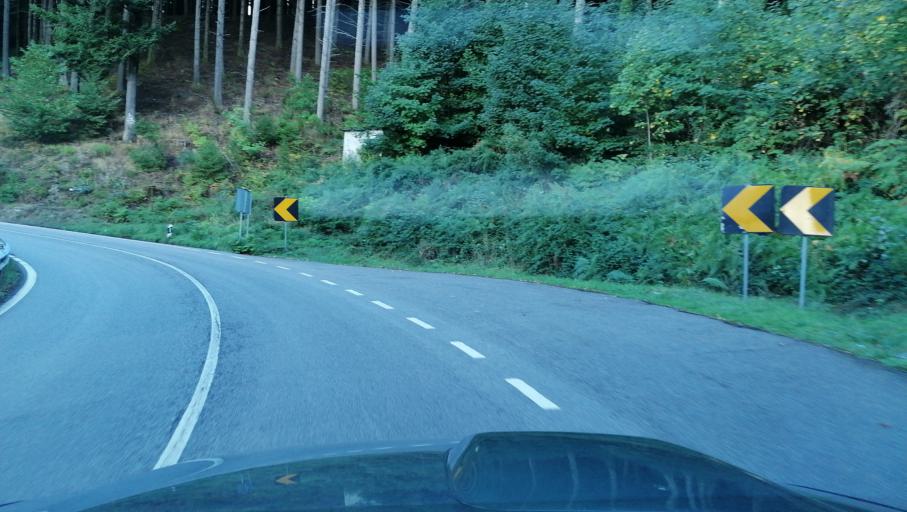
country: PT
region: Vila Real
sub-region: Vila Pouca de Aguiar
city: Vila Pouca de Aguiar
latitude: 41.5049
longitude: -7.6307
